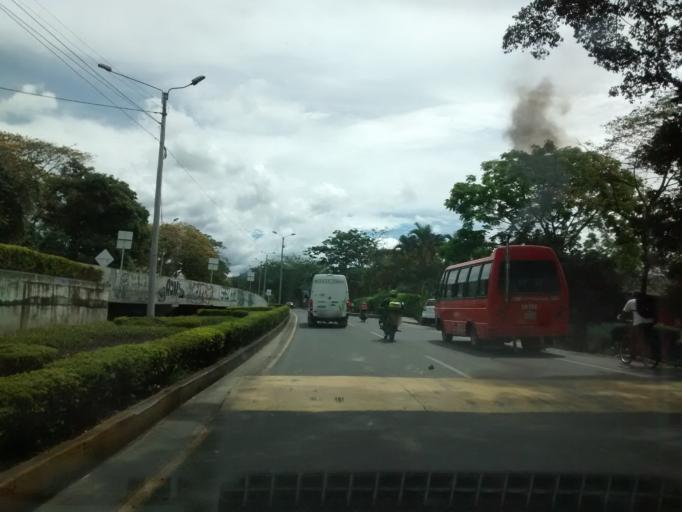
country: CO
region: Tolima
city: Ibague
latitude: 4.4037
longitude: -75.1543
